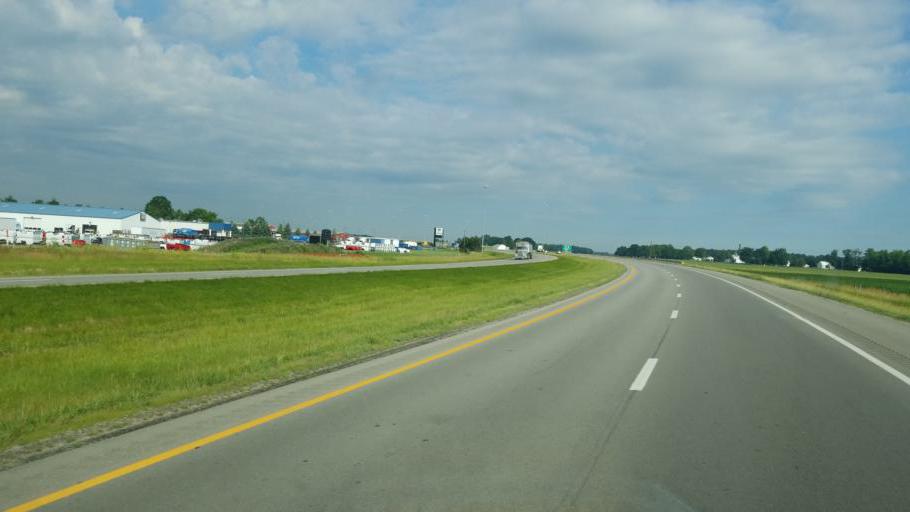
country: US
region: Ohio
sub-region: Wyandot County
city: Upper Sandusky
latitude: 40.8567
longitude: -83.2687
